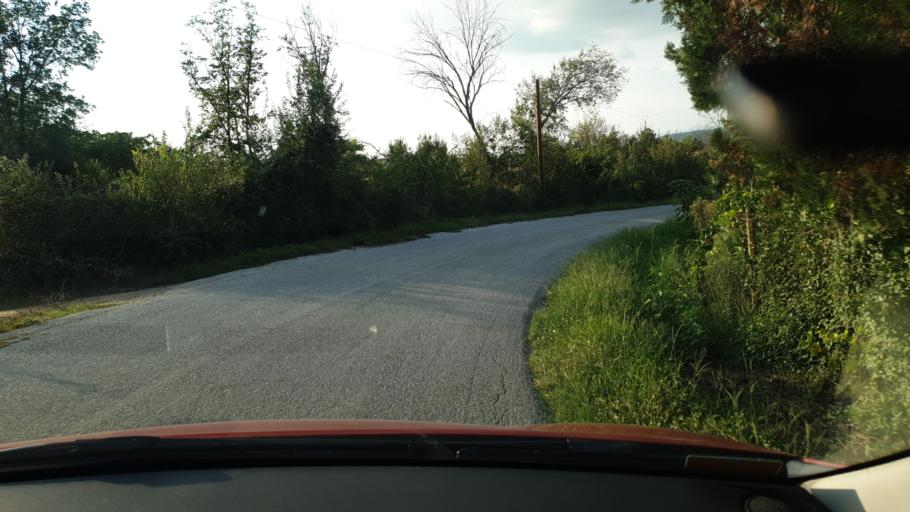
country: GR
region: Central Macedonia
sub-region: Nomos Chalkidikis
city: Galatista
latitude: 40.5603
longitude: 23.2816
